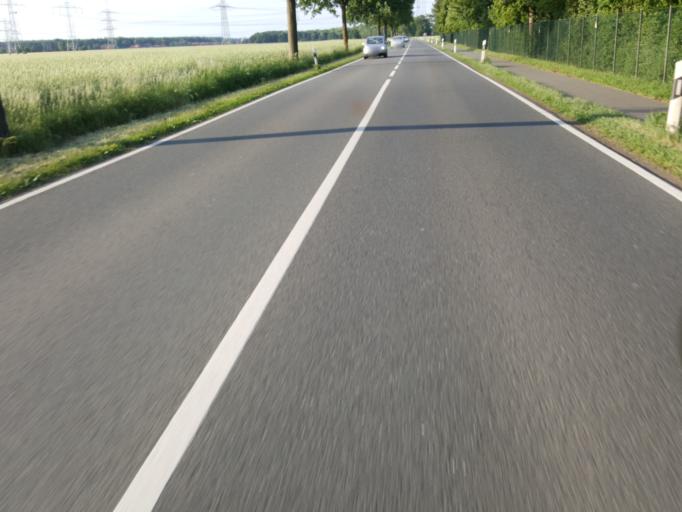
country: DE
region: Lower Saxony
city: Landesbergen
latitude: 52.5449
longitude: 9.1166
